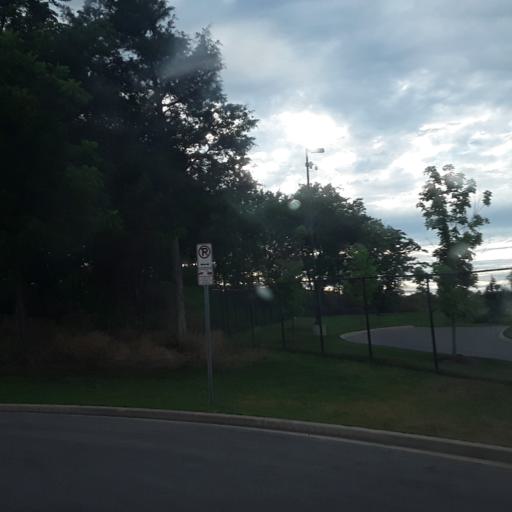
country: US
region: Tennessee
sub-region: Wilson County
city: Green Hill
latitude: 36.1674
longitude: -86.5970
